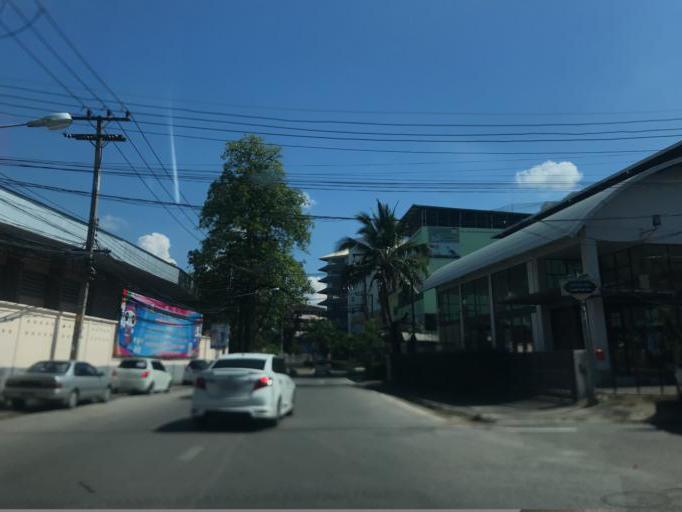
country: TH
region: Chiang Mai
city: Chiang Mai
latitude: 18.8001
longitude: 98.9878
